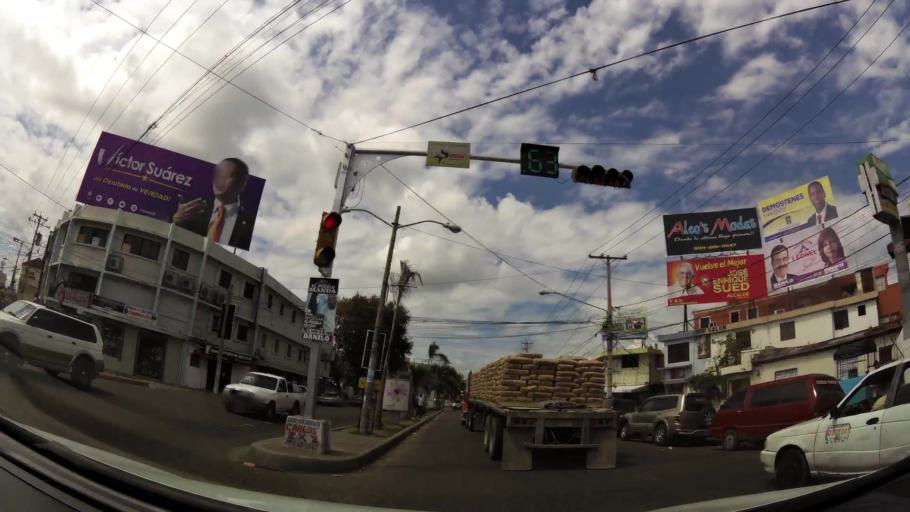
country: DO
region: Santiago
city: Santiago de los Caballeros
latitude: 19.4561
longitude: -70.7025
